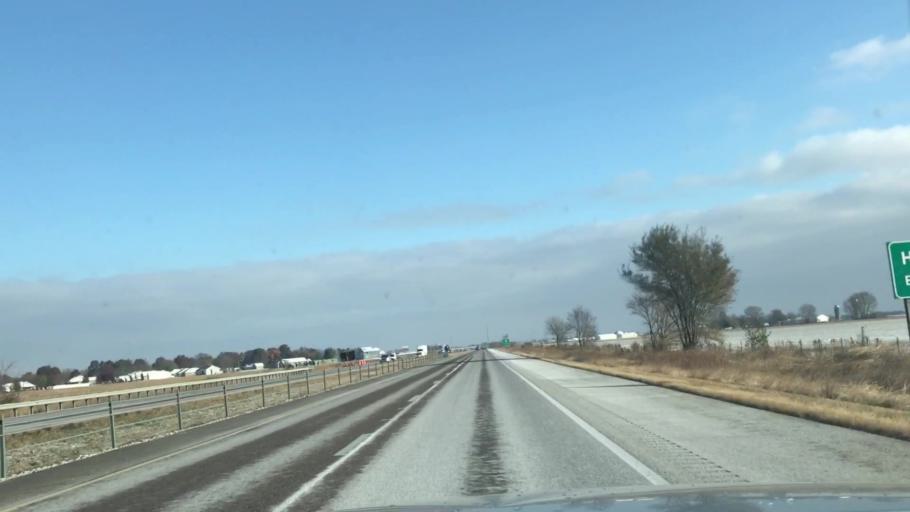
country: US
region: Illinois
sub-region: Madison County
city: Worden
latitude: 38.8762
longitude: -89.8469
